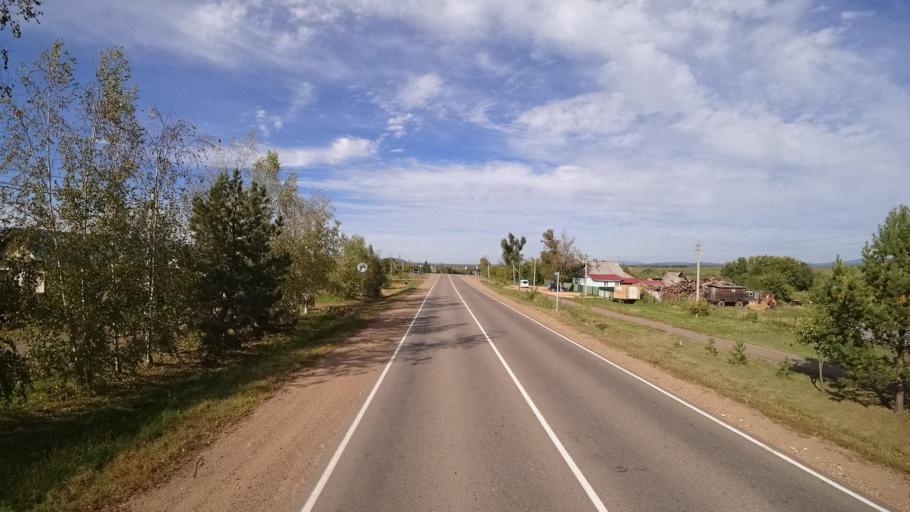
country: RU
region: Primorskiy
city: Dostoyevka
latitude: 44.3047
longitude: 133.4501
